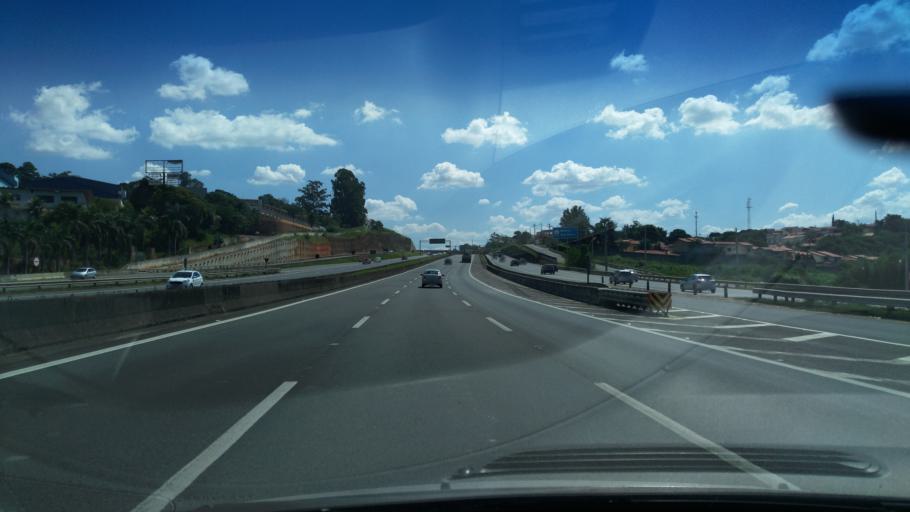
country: BR
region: Sao Paulo
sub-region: Campinas
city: Campinas
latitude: -22.8437
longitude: -47.0457
